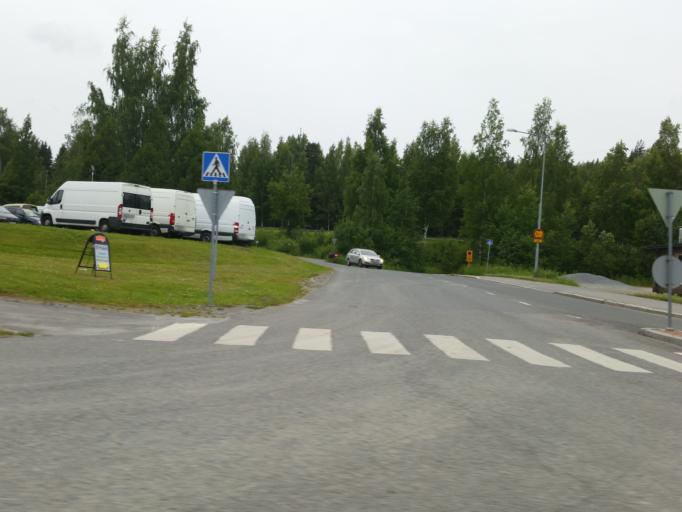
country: FI
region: Northern Savo
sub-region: Kuopio
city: Kuopio
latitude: 62.8730
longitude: 27.6230
